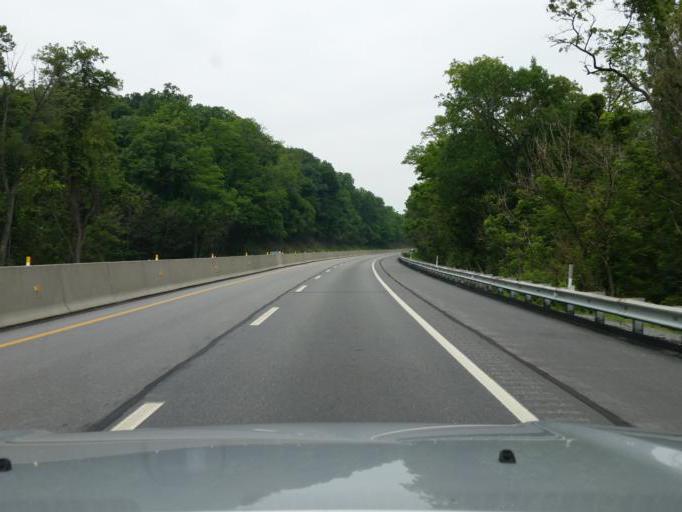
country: US
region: Pennsylvania
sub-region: Cumberland County
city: Shiremanstown
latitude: 40.1957
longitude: -76.9295
